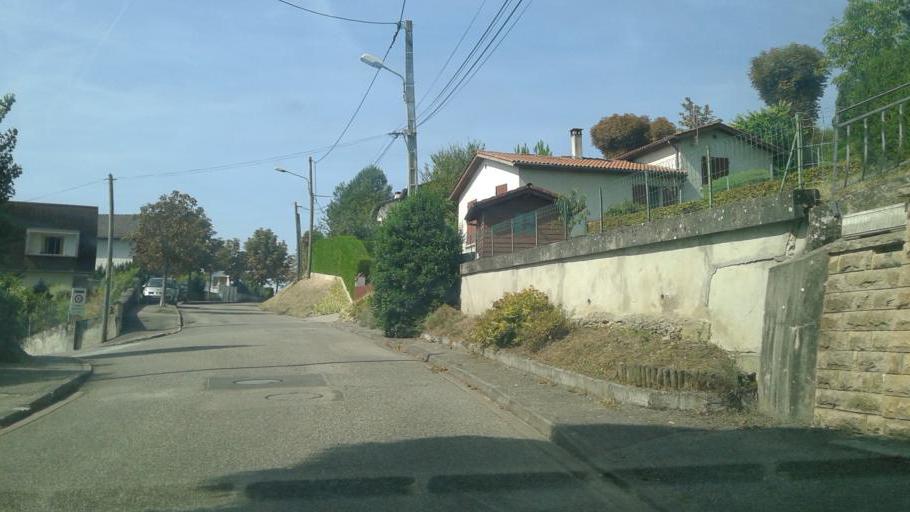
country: FR
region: Rhone-Alpes
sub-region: Departement de l'Ain
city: Montluel
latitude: 45.8513
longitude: 5.0509
